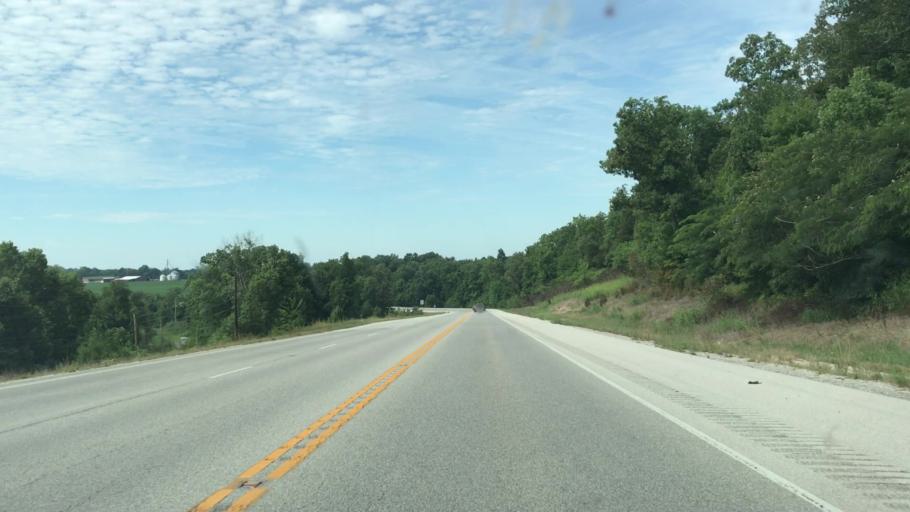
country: US
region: Kentucky
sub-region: Edmonson County
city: Brownsville
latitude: 37.0975
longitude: -86.2317
